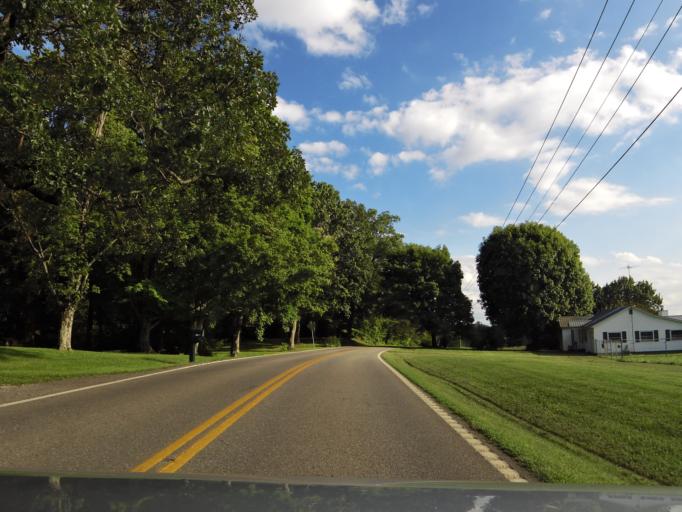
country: US
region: Tennessee
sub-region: Loudon County
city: Greenback
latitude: 35.6345
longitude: -84.0994
